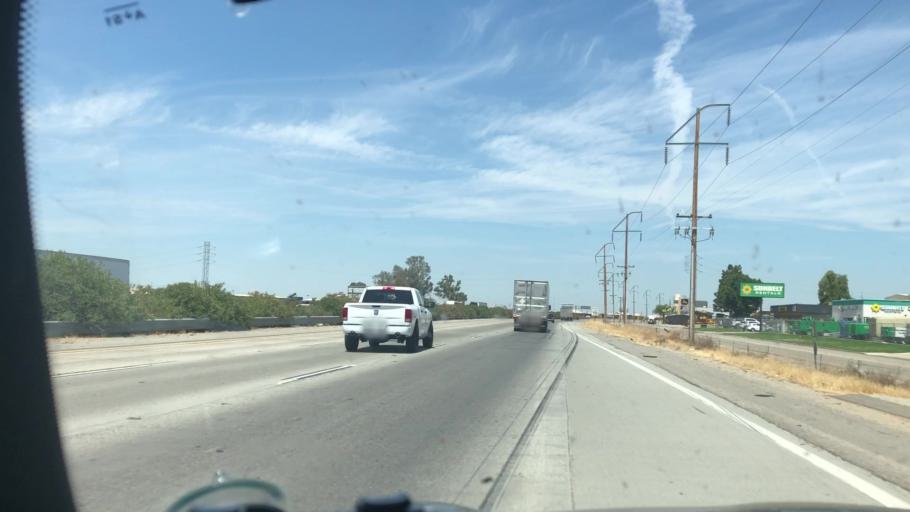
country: US
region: California
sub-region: Kern County
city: Greenacres
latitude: 35.4439
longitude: -119.0884
